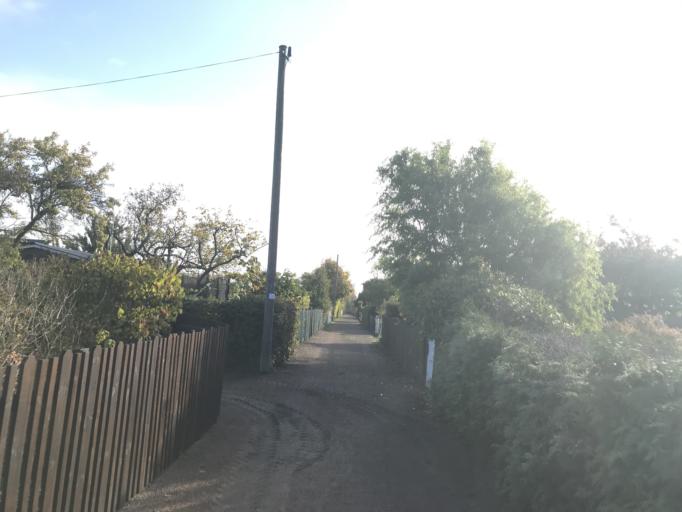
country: SE
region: Skane
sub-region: Landskrona
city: Landskrona
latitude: 55.8861
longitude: 12.8228
